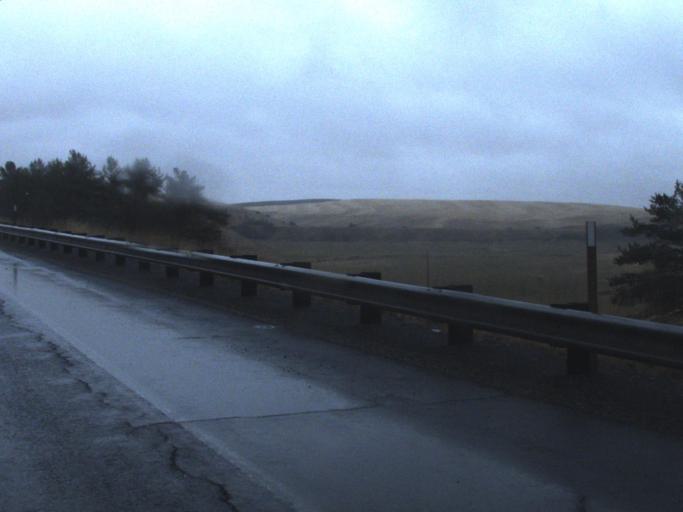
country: US
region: Washington
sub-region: Whitman County
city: Colfax
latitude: 47.2134
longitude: -117.3593
